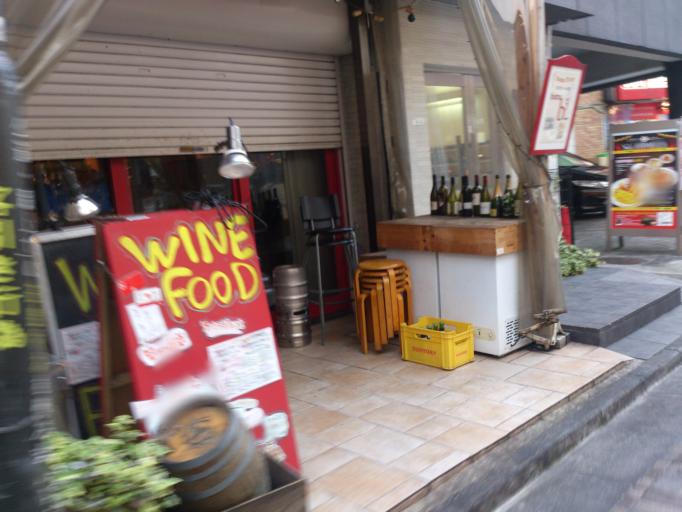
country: JP
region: Tokyo
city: Tokyo
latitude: 35.6474
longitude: 139.7106
